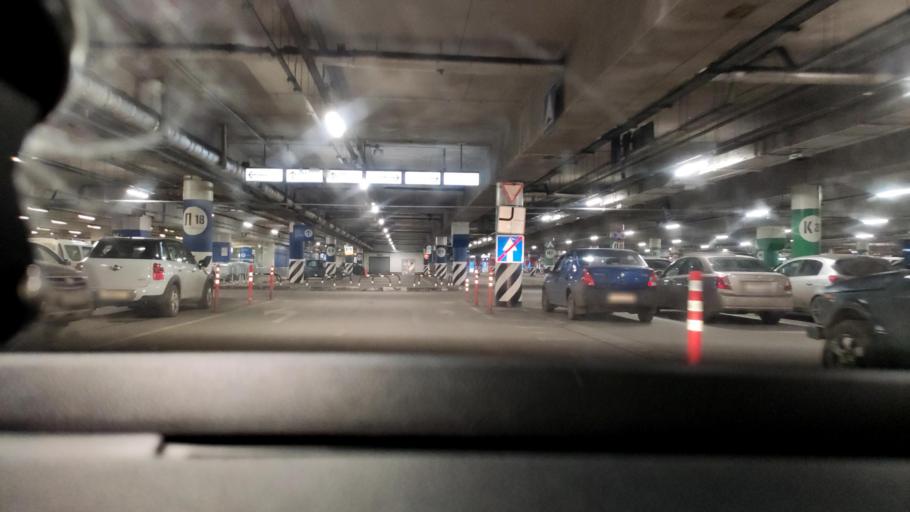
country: RU
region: Moskovskaya
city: Kotel'niki
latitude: 55.6542
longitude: 37.8466
